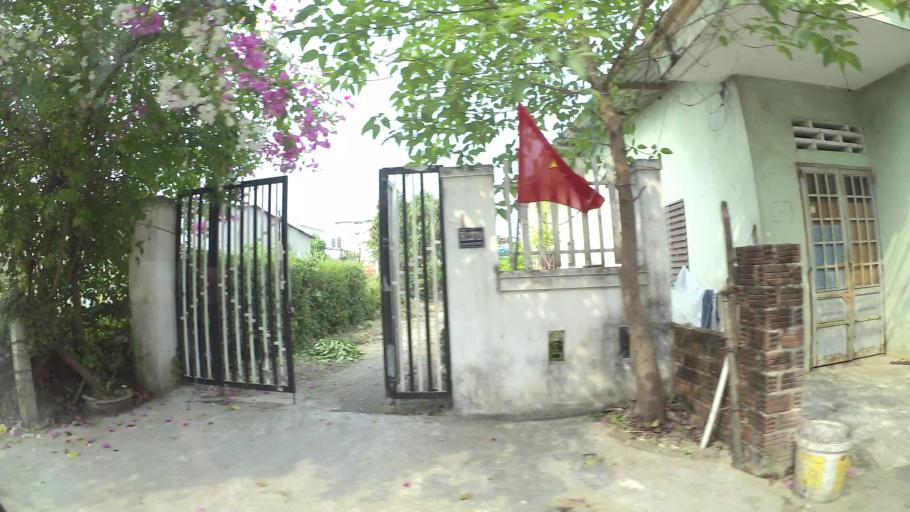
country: VN
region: Da Nang
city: Lien Chieu
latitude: 16.0589
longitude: 108.1579
